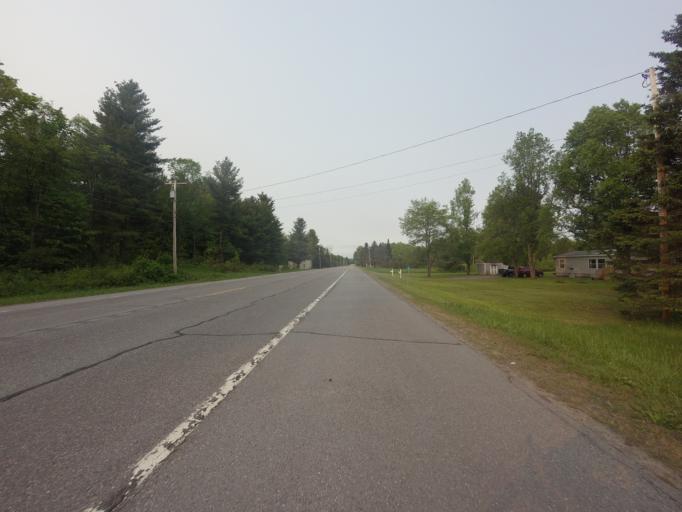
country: US
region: New York
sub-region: Jefferson County
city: Carthage
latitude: 44.0857
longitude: -75.4317
